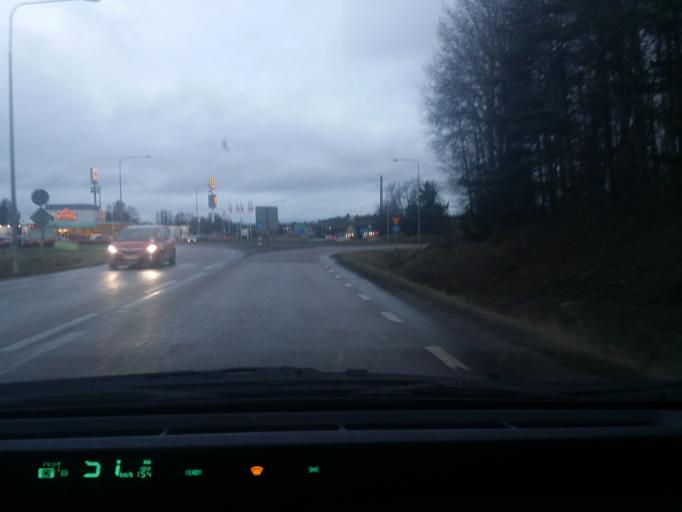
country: SE
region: Soedermanland
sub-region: Eskilstuna Kommun
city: Torshalla
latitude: 59.3907
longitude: 16.4665
